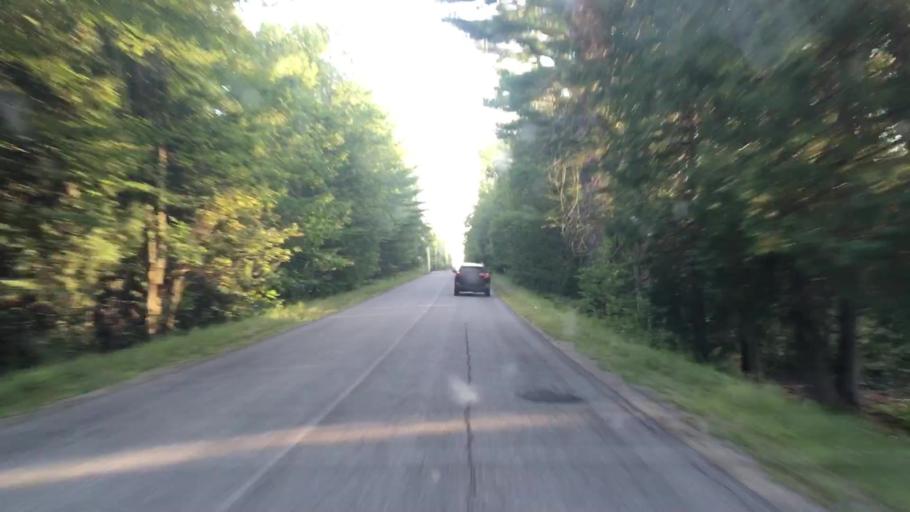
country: US
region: Maine
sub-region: Waldo County
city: Winterport
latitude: 44.6833
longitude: -68.9108
